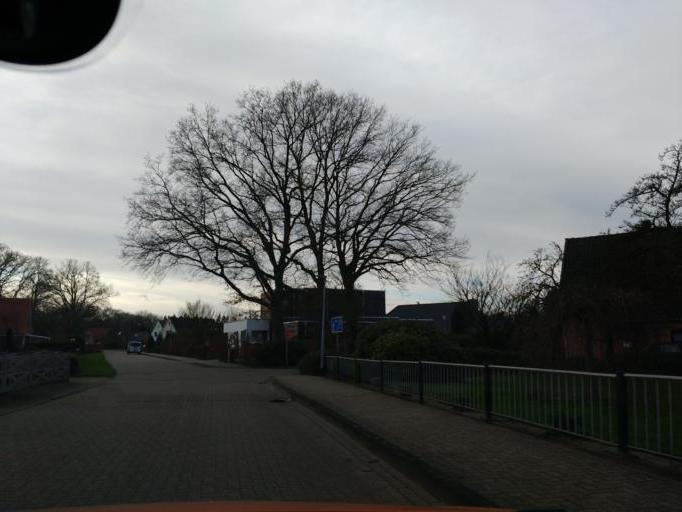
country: DE
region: Lower Saxony
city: Hude
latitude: 53.0980
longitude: 8.4627
